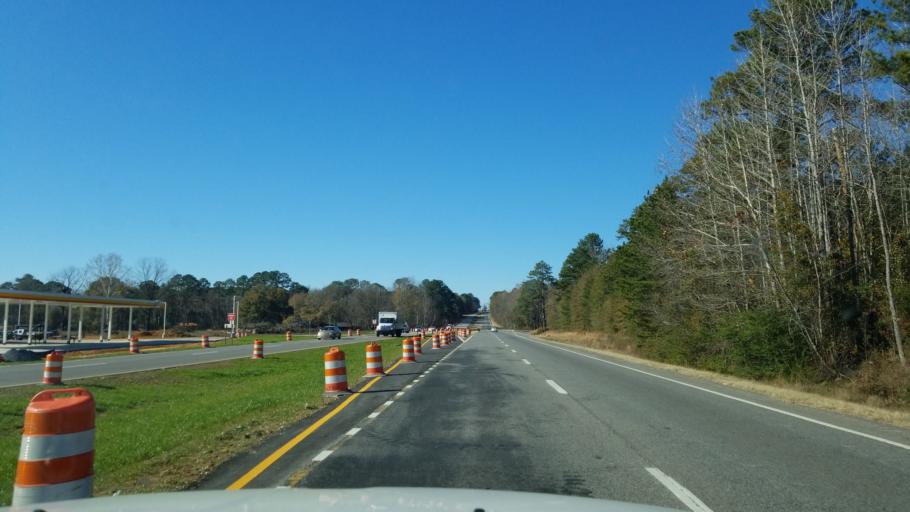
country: US
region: Alabama
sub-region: Tuscaloosa County
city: Northport
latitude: 33.2457
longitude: -87.6731
